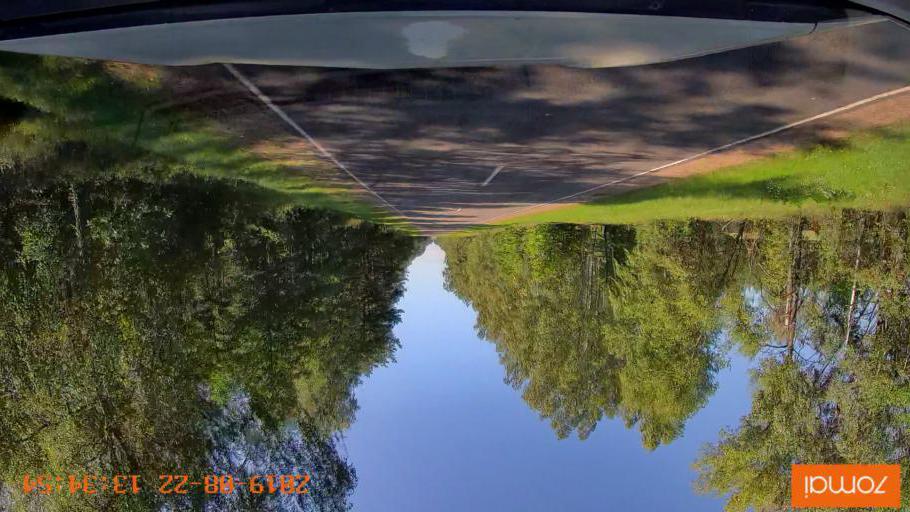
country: BY
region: Minsk
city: Staryya Darohi
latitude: 53.2145
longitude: 28.2535
